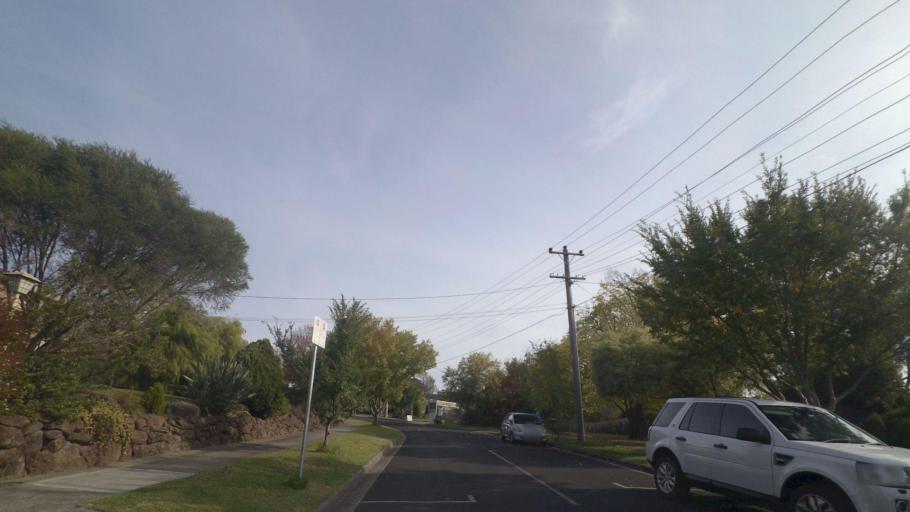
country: AU
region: Victoria
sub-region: Manningham
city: Doncaster East
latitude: -37.7802
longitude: 145.1538
